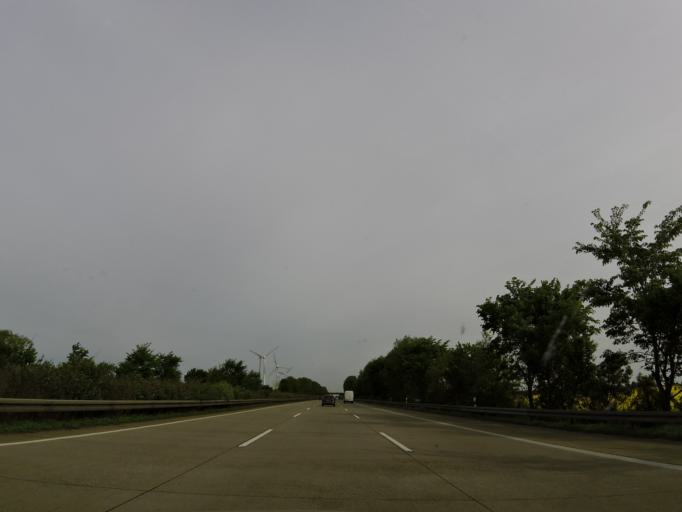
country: DE
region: Lower Saxony
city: Algermissen
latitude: 52.2593
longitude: 9.9179
